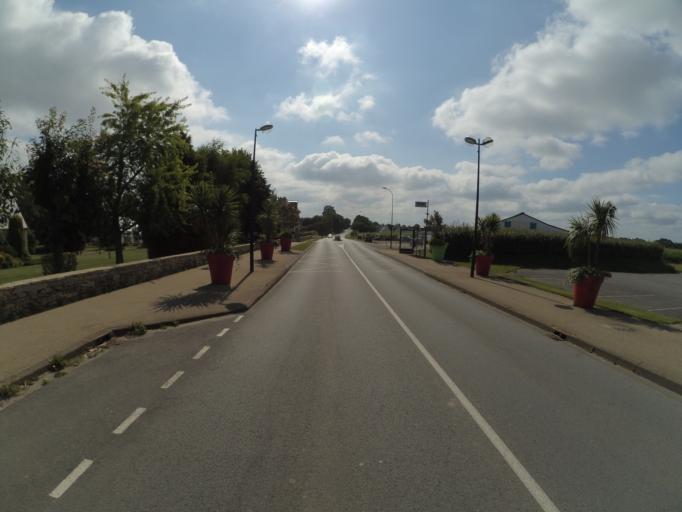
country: FR
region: Brittany
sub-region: Departement du Finistere
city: Mellac
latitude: 47.9003
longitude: -3.5826
